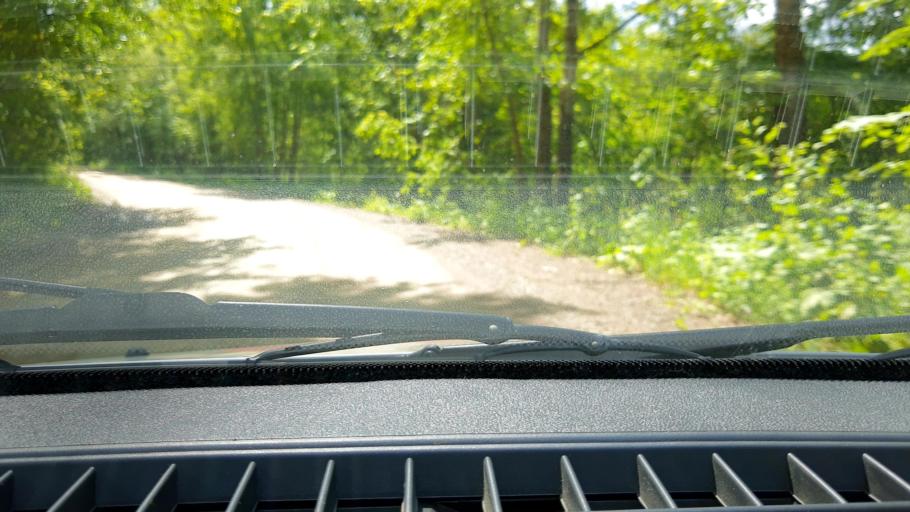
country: RU
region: Bashkortostan
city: Ufa
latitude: 54.6785
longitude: 56.0610
